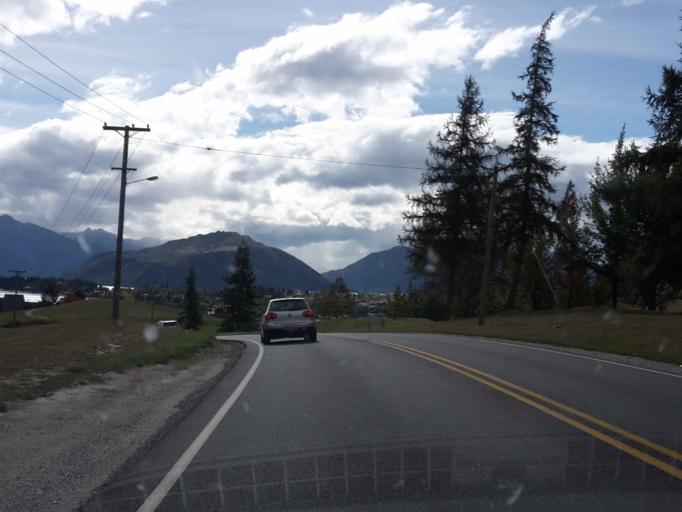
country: NZ
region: Otago
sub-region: Queenstown-Lakes District
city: Wanaka
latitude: -44.7065
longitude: 169.1359
